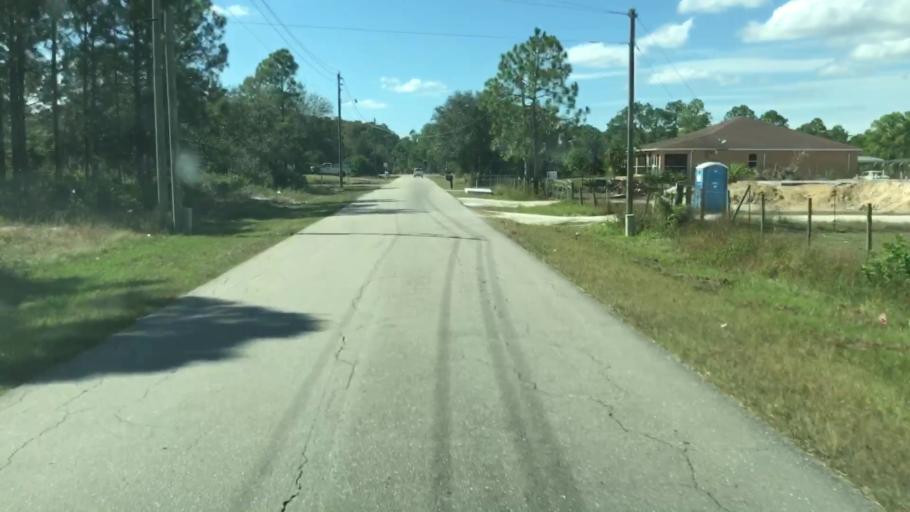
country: US
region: Florida
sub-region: Lee County
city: Alva
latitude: 26.6835
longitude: -81.5959
